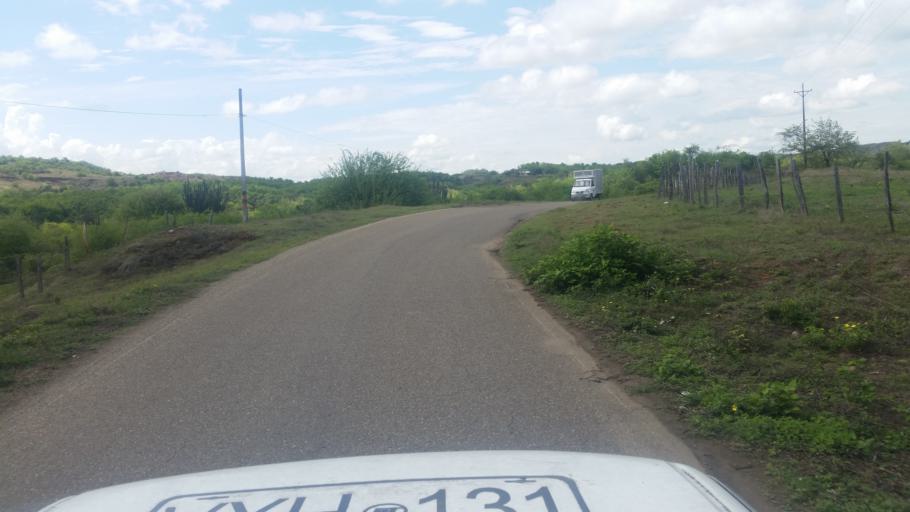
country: CO
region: Huila
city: Villavieja
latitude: 3.1946
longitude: -75.2138
